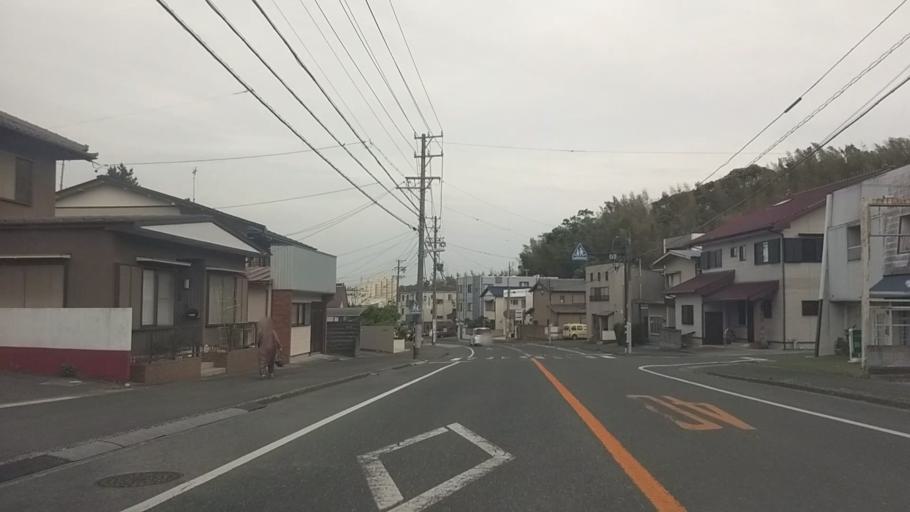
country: JP
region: Shizuoka
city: Hamamatsu
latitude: 34.7263
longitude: 137.6935
